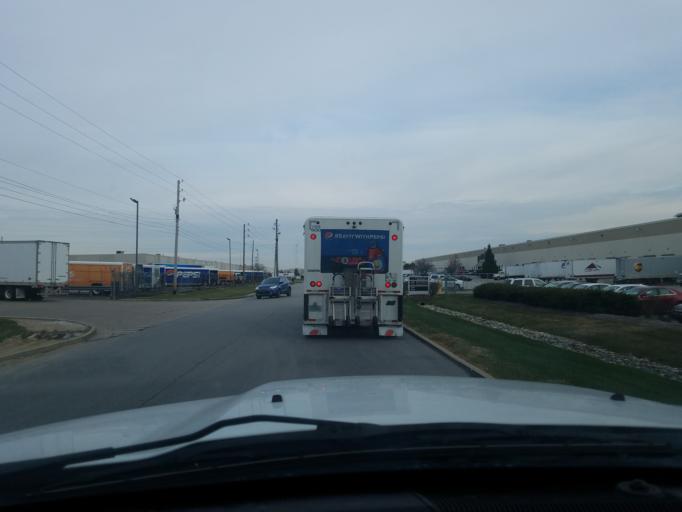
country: US
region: Indiana
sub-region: Boone County
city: Zionsville
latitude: 39.8909
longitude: -86.2554
